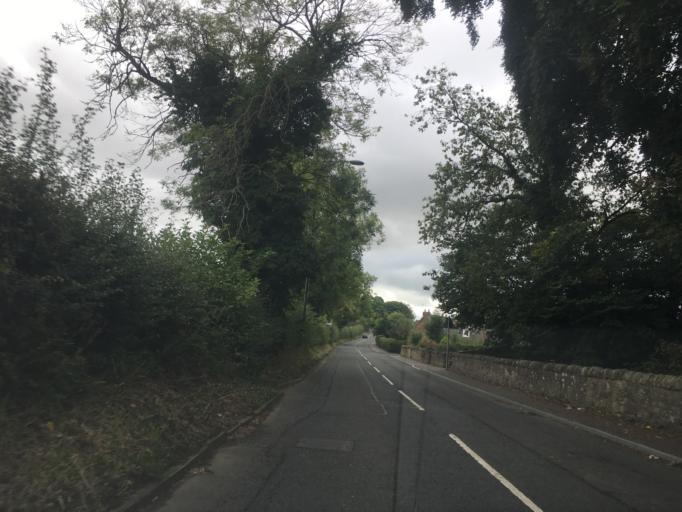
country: GB
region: Scotland
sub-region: Midlothian
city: Dalkeith
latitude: 55.8756
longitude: -3.0677
